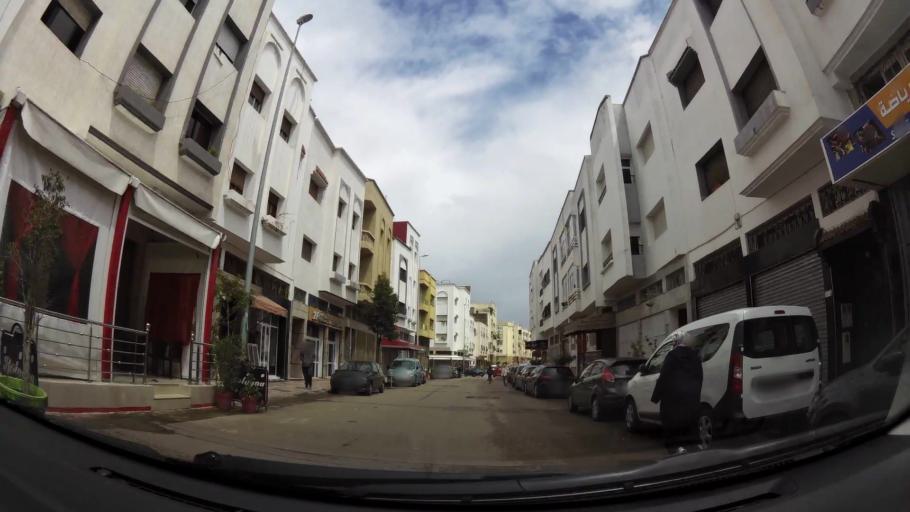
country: MA
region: Grand Casablanca
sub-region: Casablanca
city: Casablanca
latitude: 33.5445
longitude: -7.6779
